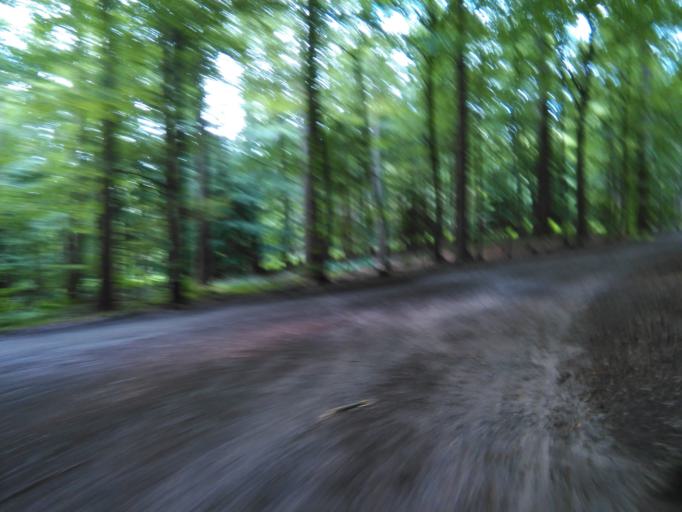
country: DK
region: Central Jutland
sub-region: Arhus Kommune
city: Arhus
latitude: 56.1168
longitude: 10.2199
